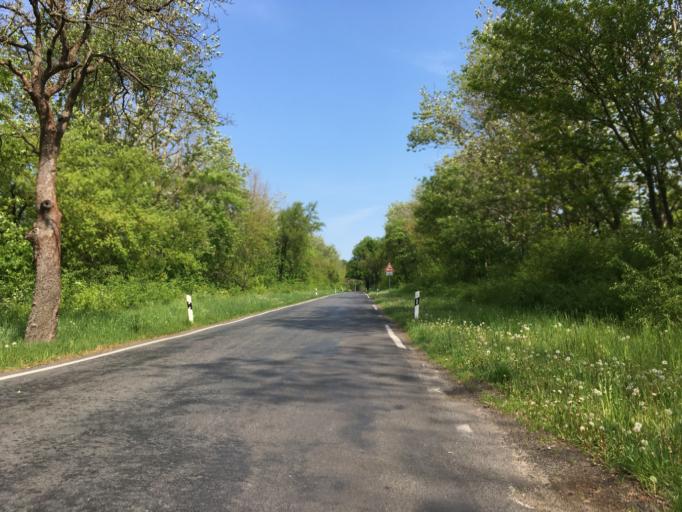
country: DE
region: Brandenburg
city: Werneuchen
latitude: 52.6623
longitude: 13.7314
